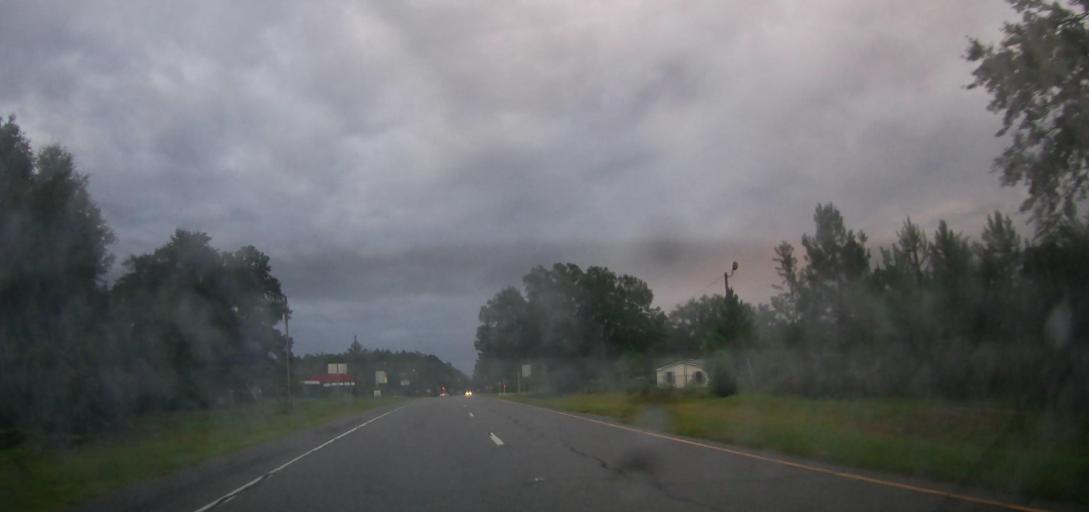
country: US
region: Georgia
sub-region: Lanier County
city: Lakeland
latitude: 30.9356
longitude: -83.0102
